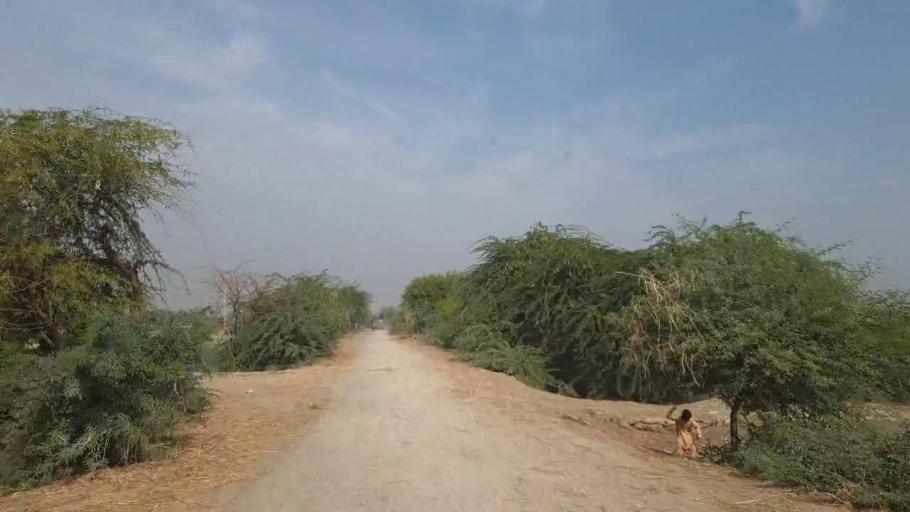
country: PK
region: Sindh
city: Tando Bago
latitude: 24.9122
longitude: 68.9961
